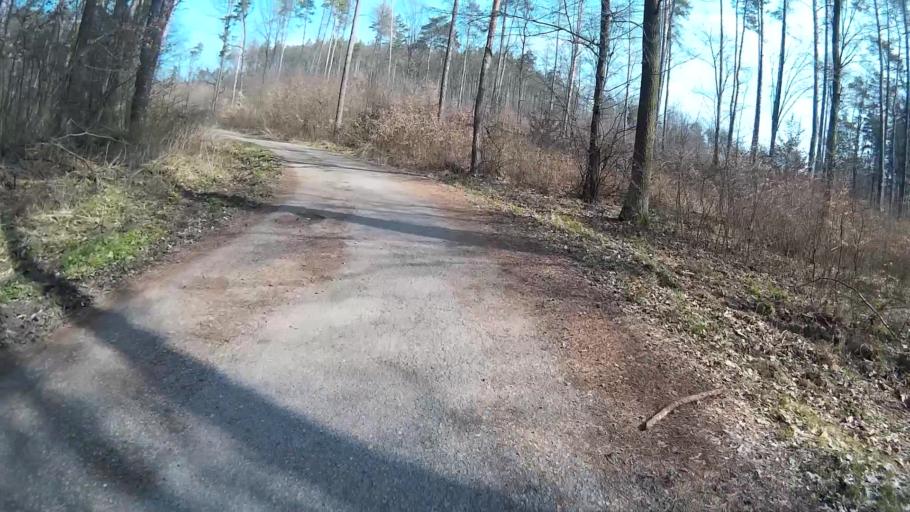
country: CZ
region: South Moravian
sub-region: Mesto Brno
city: Mokra Hora
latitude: 49.2559
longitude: 16.6083
